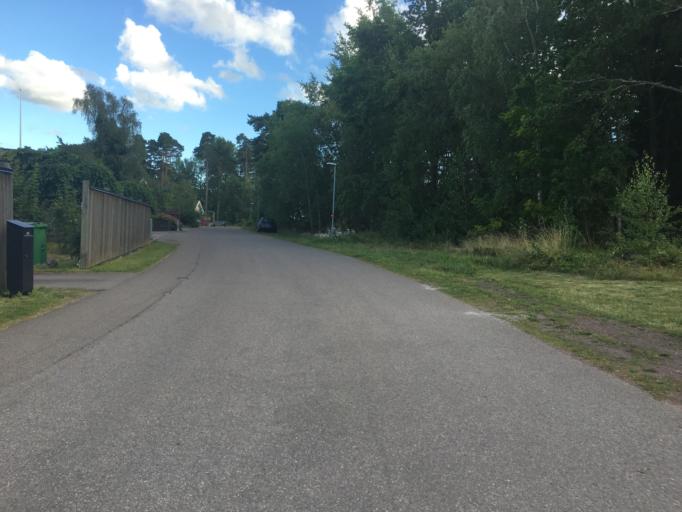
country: SE
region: Kalmar
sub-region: Kalmar Kommun
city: Kalmar
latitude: 56.7029
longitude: 16.3721
